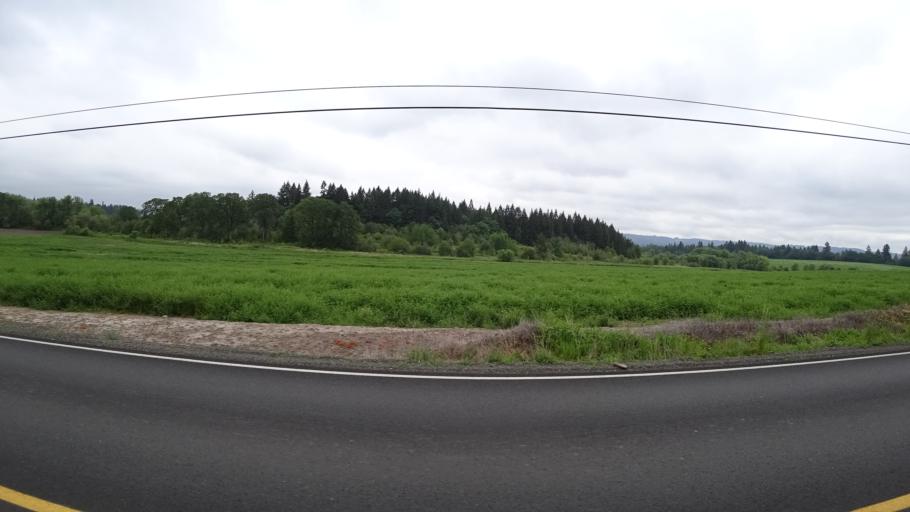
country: US
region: Oregon
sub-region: Washington County
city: Rockcreek
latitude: 45.5641
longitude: -122.8901
